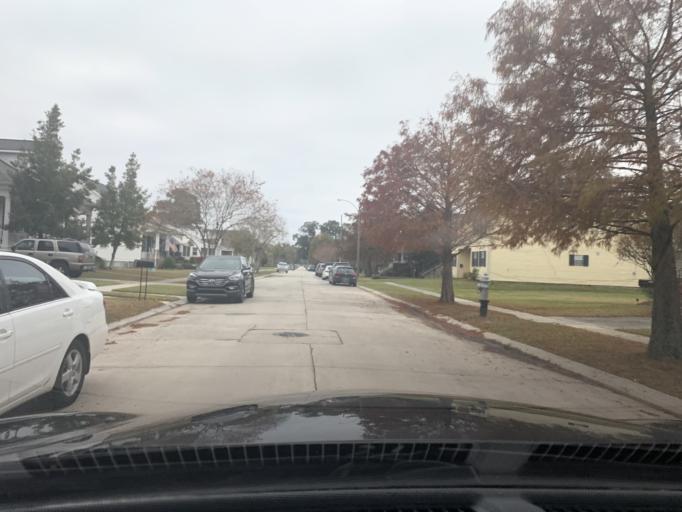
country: US
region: Louisiana
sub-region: Jefferson Parish
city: Metairie
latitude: 30.0042
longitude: -90.1115
